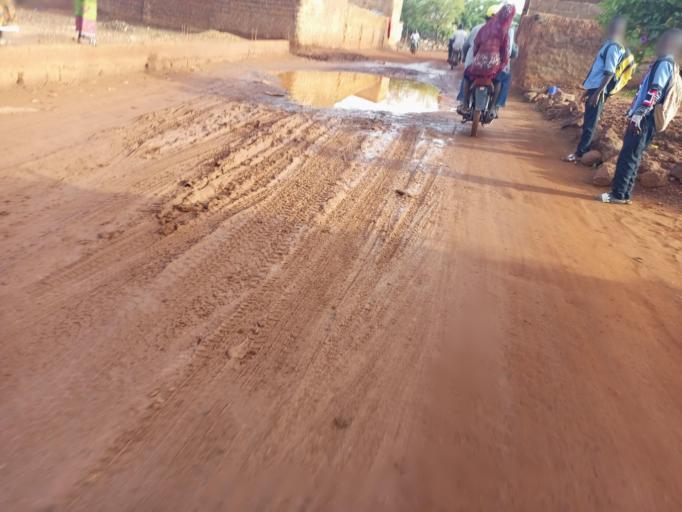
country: ML
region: Bamako
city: Bamako
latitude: 12.5215
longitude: -7.9940
